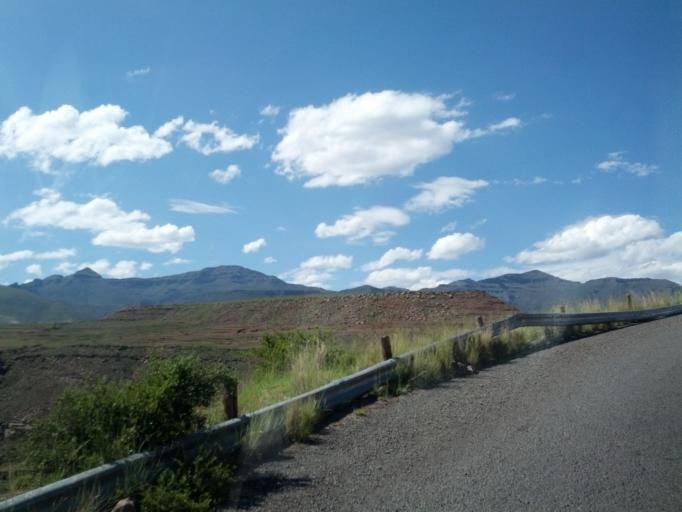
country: LS
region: Qacha's Nek
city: Qacha's Nek
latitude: -30.0679
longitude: 28.4596
